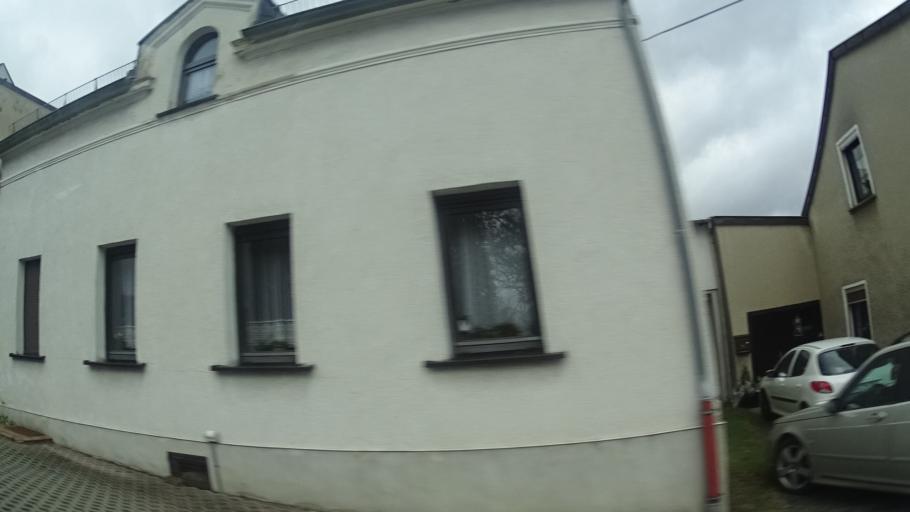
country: DE
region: Thuringia
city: Zeulenroda
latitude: 50.6442
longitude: 11.9862
